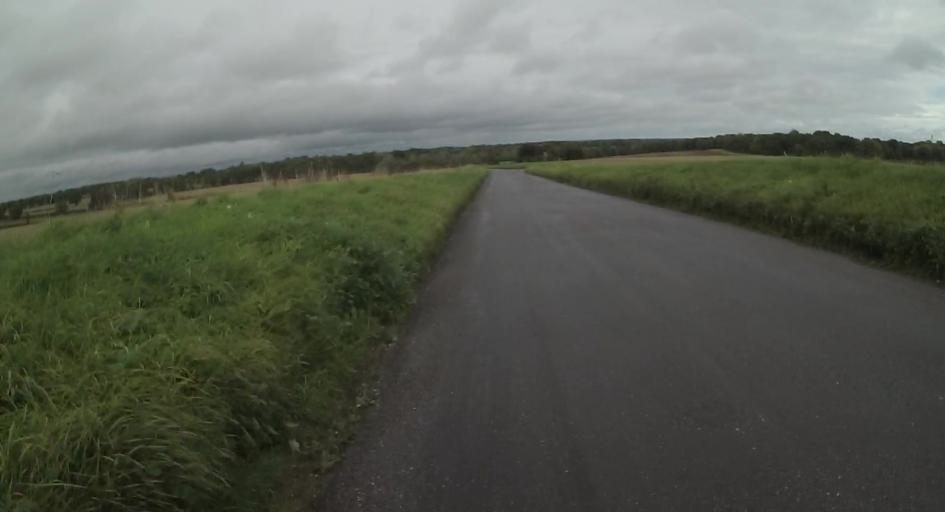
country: GB
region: England
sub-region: Hampshire
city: Tadley
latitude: 51.2991
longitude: -1.1527
